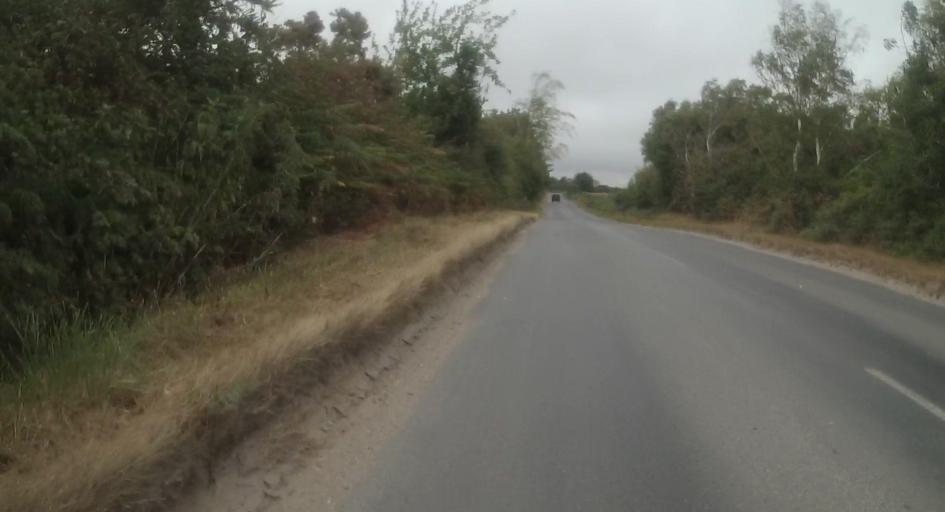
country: GB
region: England
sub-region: Dorset
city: Wool
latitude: 50.6969
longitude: -2.1856
